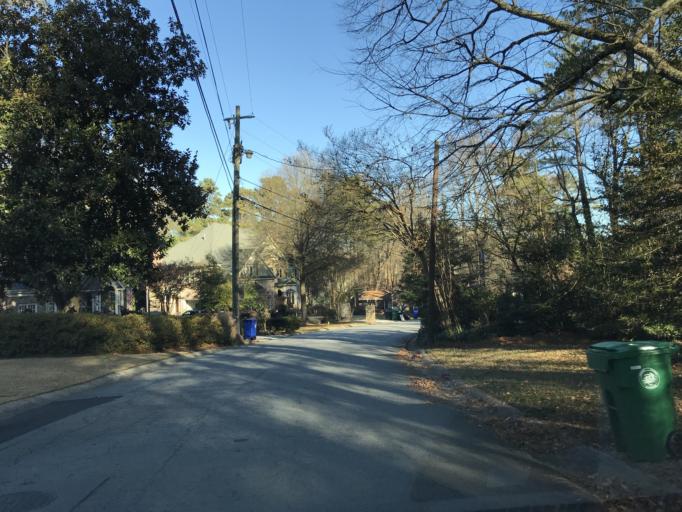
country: US
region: Georgia
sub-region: DeKalb County
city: North Atlanta
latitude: 33.8860
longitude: -84.3392
